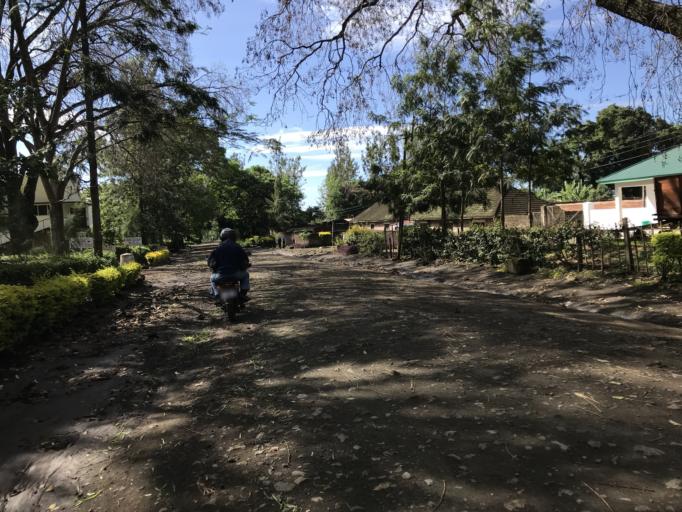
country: TZ
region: Arusha
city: Nkoaranga
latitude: -3.3843
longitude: 36.7959
